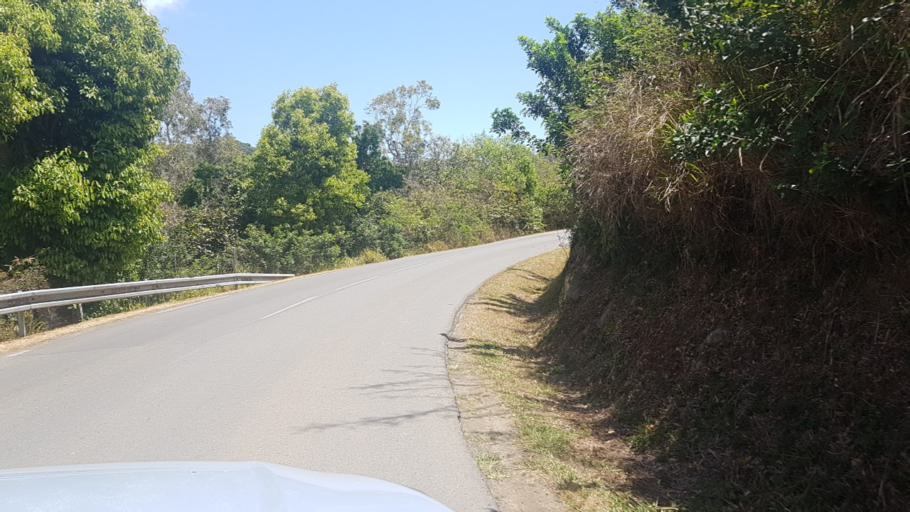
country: NC
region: South Province
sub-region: Dumbea
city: Dumbea
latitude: -22.1389
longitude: 166.4436
